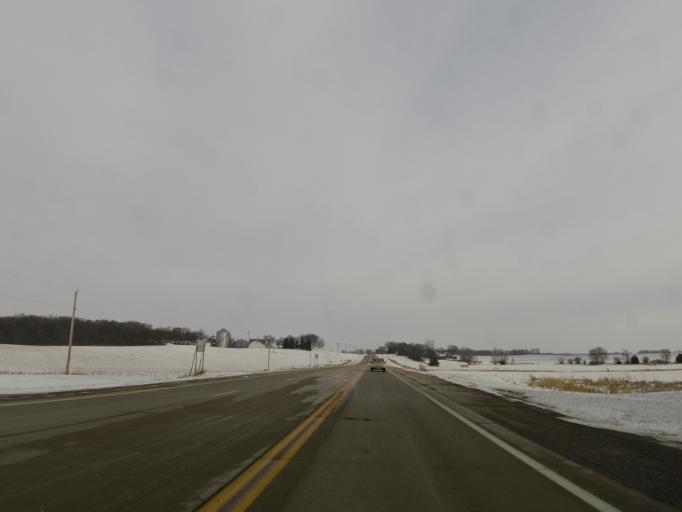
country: US
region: Minnesota
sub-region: McLeod County
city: Hutchinson
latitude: 44.8926
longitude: -94.2422
